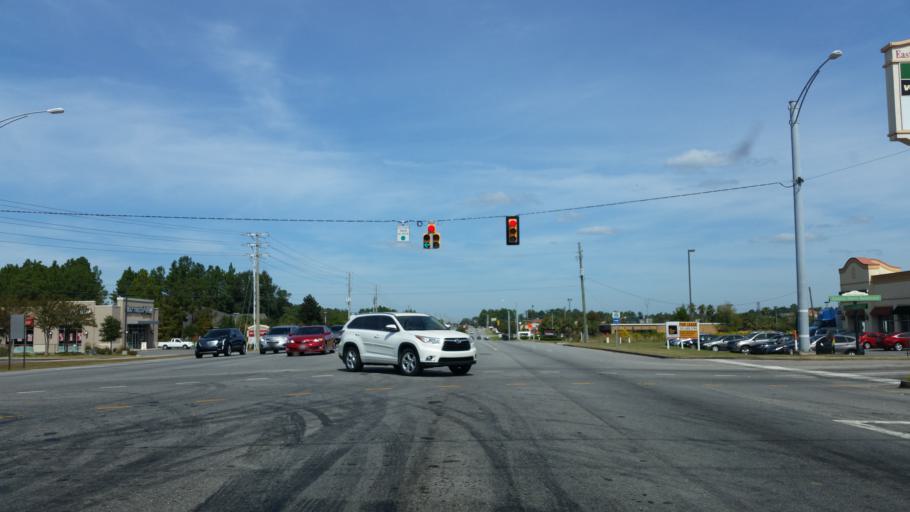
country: US
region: Alabama
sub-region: Baldwin County
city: Spanish Fort
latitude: 30.6665
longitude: -87.8521
